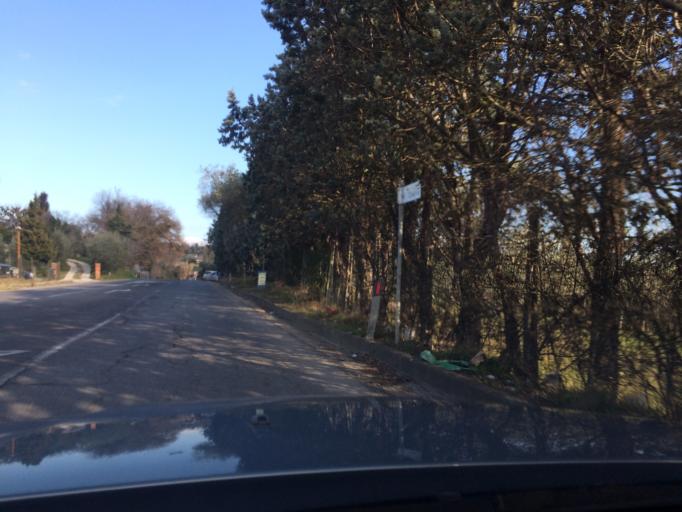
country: IT
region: Umbria
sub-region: Provincia di Terni
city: Amelia
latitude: 42.5573
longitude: 12.4331
